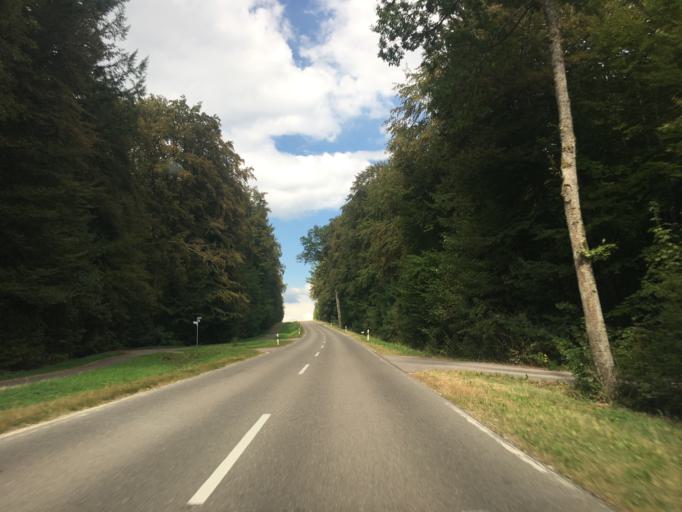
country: DE
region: Baden-Wuerttemberg
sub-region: Tuebingen Region
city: Hayingen
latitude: 48.3015
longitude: 9.4510
